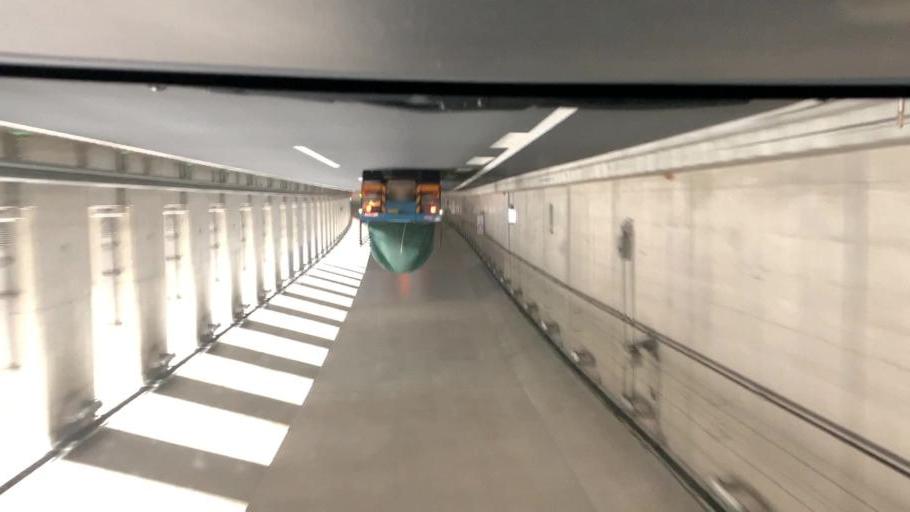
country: JP
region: Chiba
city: Matsudo
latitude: 35.7610
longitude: 139.9061
